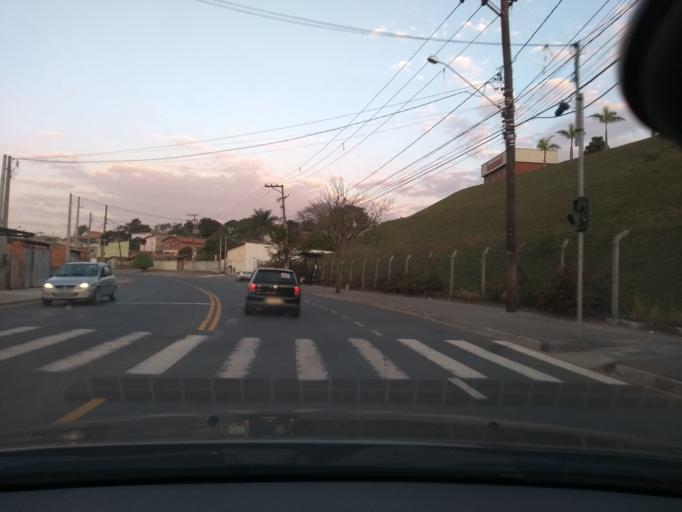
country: BR
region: Sao Paulo
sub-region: Itupeva
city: Itupeva
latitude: -23.1428
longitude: -47.0400
